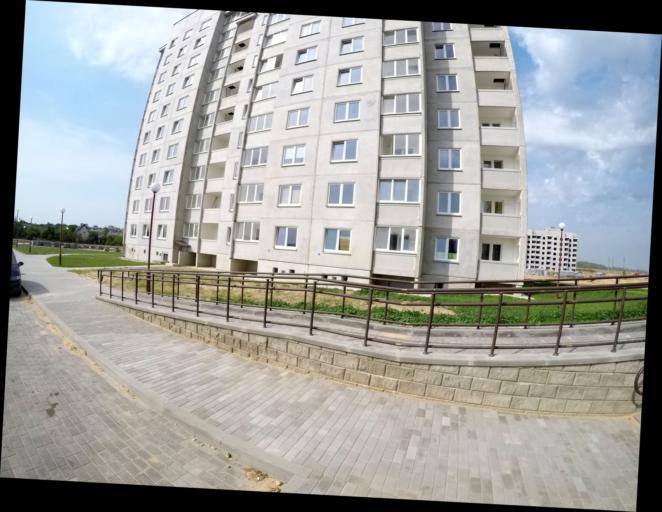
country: BY
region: Grodnenskaya
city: Hrodna
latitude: 53.7182
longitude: 23.8635
